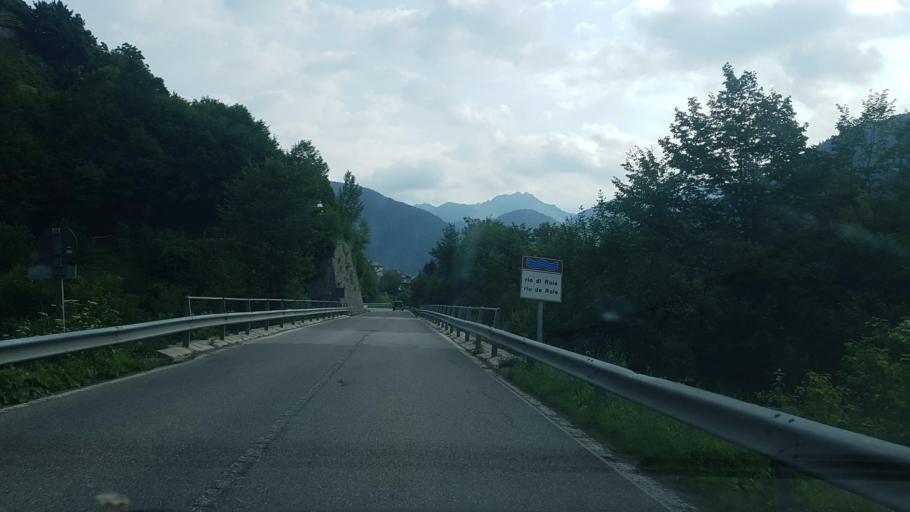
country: IT
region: Friuli Venezia Giulia
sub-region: Provincia di Udine
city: Paularo
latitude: 46.5018
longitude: 13.1125
